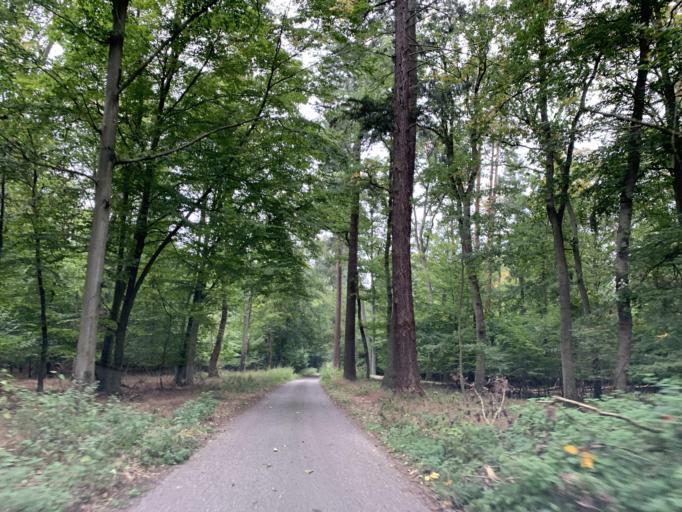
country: DE
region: Brandenburg
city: Mittenwalde
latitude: 53.3177
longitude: 13.6113
